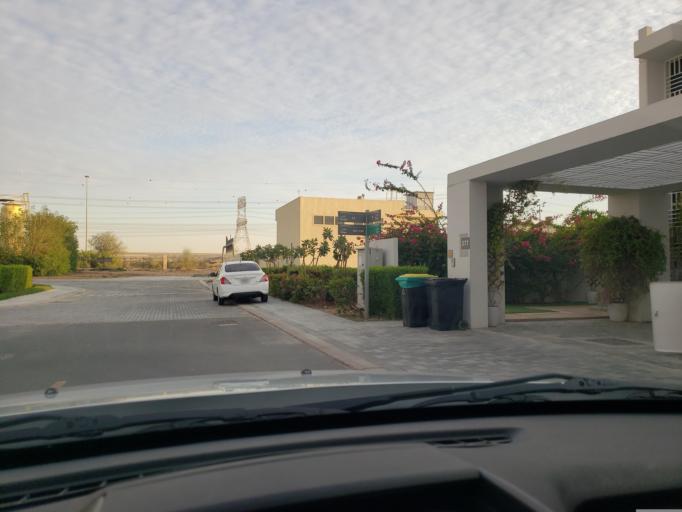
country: AE
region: Dubai
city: Dubai
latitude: 25.0141
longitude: 55.2701
